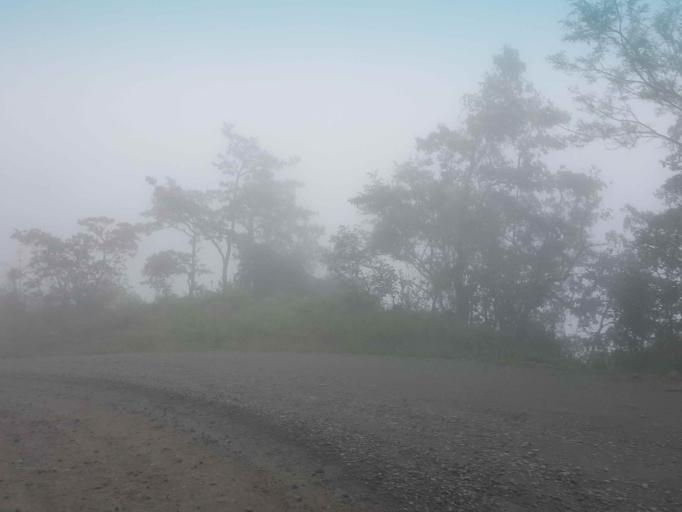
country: CR
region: Guanacaste
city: Juntas
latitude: 10.2992
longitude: -84.8355
